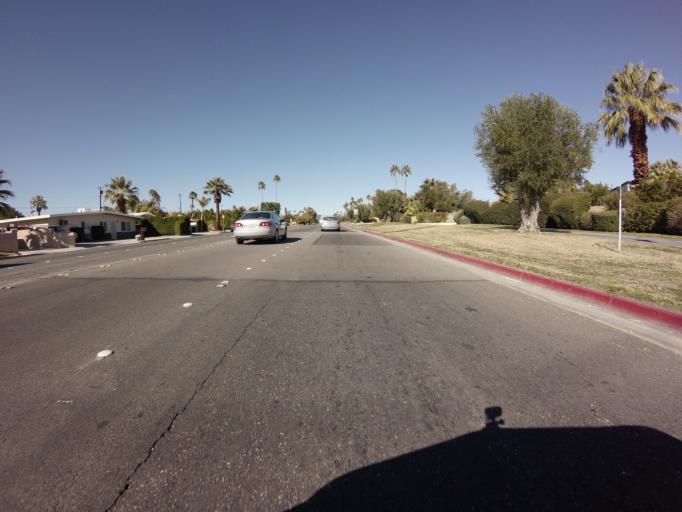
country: US
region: California
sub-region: Riverside County
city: Palm Springs
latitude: 33.8307
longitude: -116.5282
